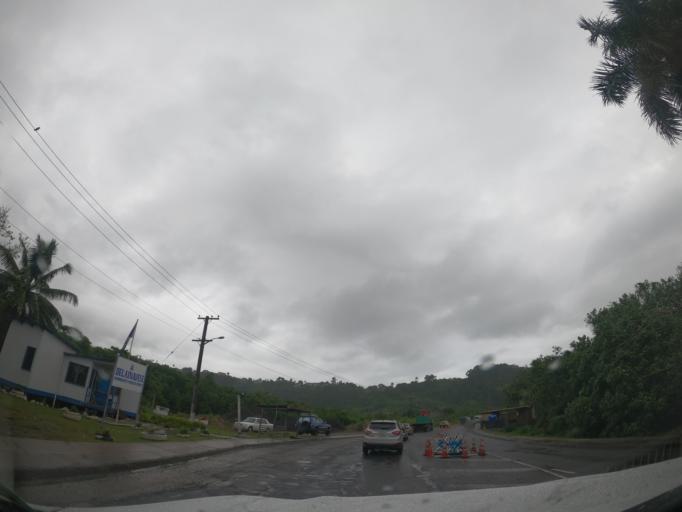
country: FJ
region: Central
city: Suva
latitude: -18.1130
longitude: 178.4300
